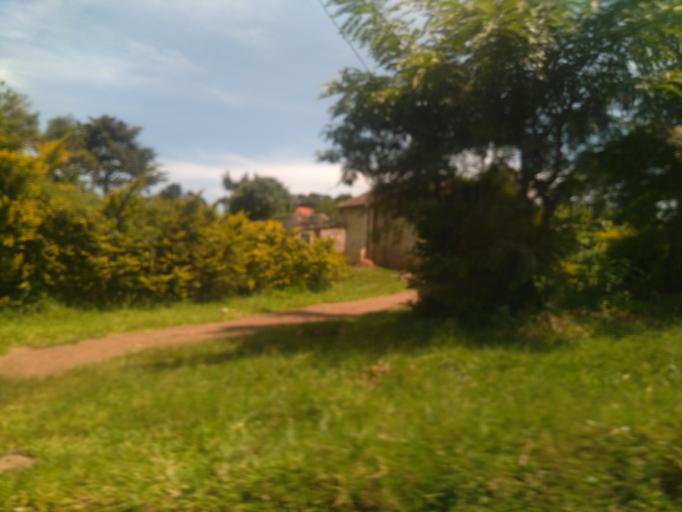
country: UG
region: Central Region
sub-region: Wakiso District
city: Entebbe
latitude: 0.0491
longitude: 32.4608
